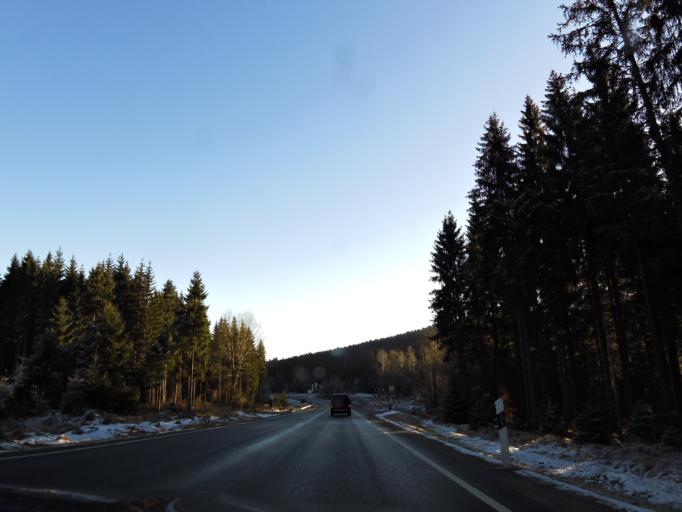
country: DE
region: Bavaria
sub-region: Upper Franconia
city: Fichtelberg
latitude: 50.0397
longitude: 11.8387
